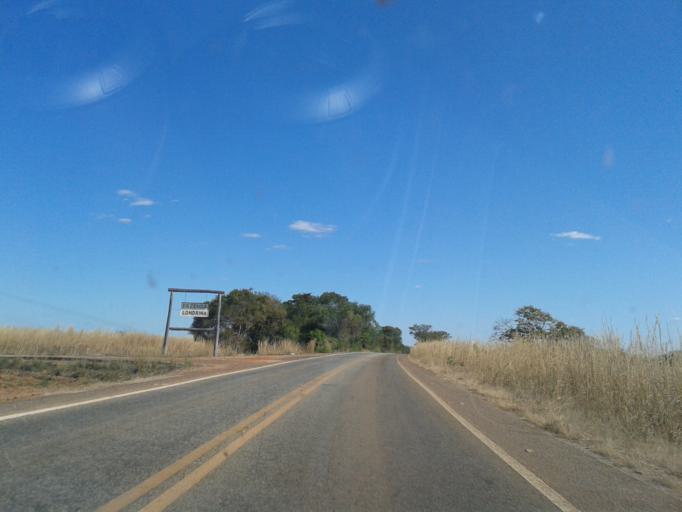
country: BR
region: Goias
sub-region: Mozarlandia
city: Mozarlandia
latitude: -14.4673
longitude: -50.4688
